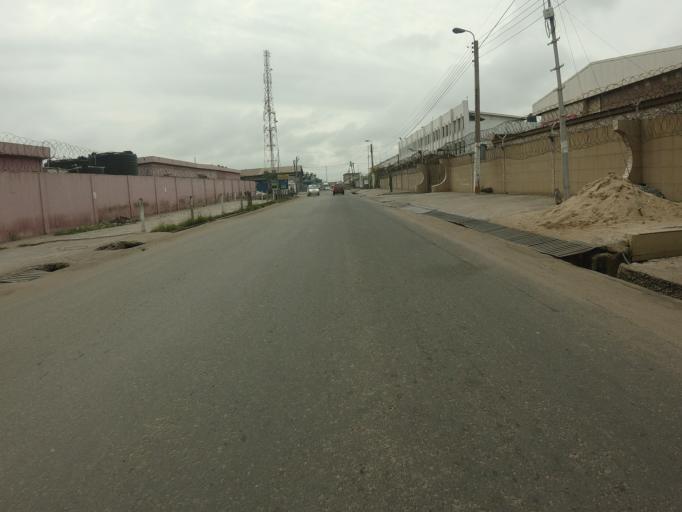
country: GH
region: Greater Accra
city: Accra
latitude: 5.5554
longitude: -0.2243
